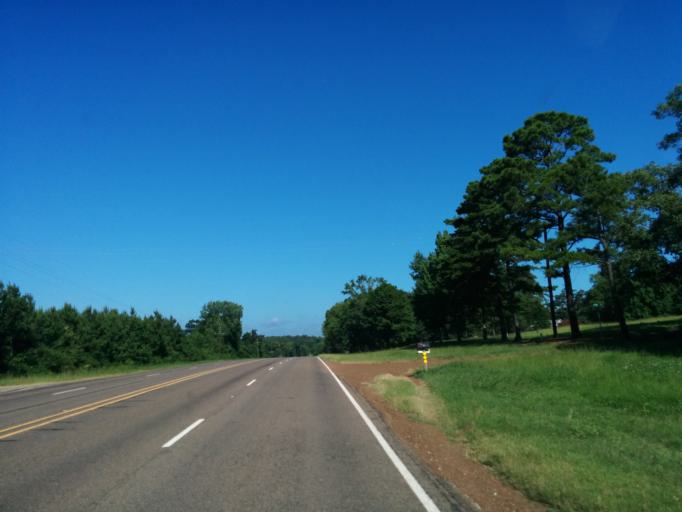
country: US
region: Texas
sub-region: Sabine County
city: Milam
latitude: 31.4316
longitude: -93.8274
